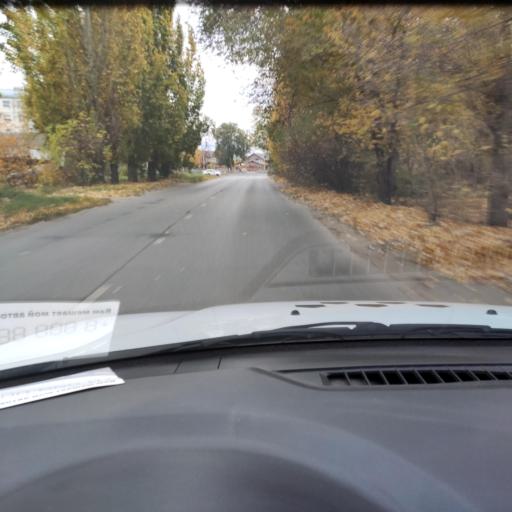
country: RU
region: Samara
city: Tol'yatti
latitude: 53.5328
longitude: 49.4182
